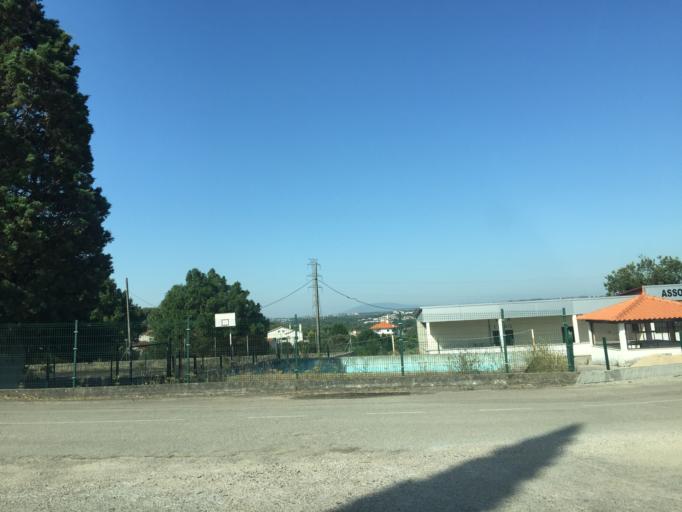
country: PT
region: Santarem
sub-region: Tomar
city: Tomar
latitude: 39.6534
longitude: -8.3826
